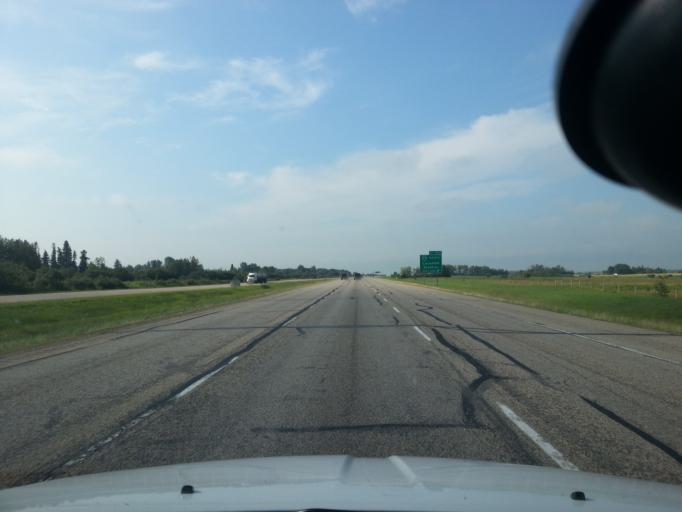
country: CA
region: Alberta
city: Lacombe
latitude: 52.5297
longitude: -113.6746
